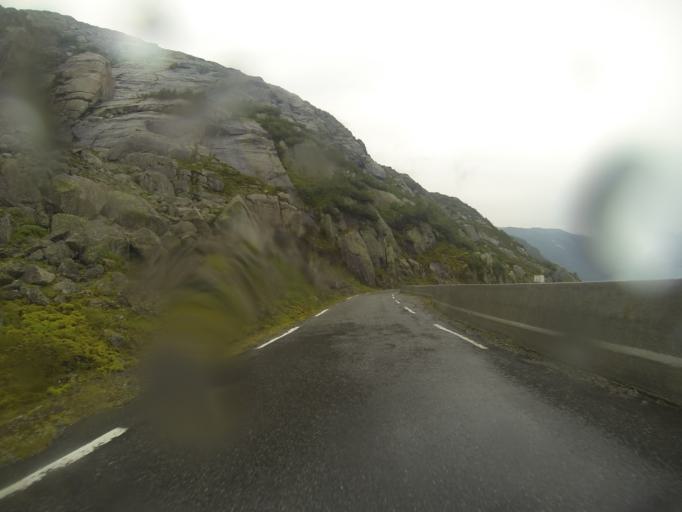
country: NO
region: Hordaland
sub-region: Odda
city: Odda
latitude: 59.7825
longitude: 6.7538
